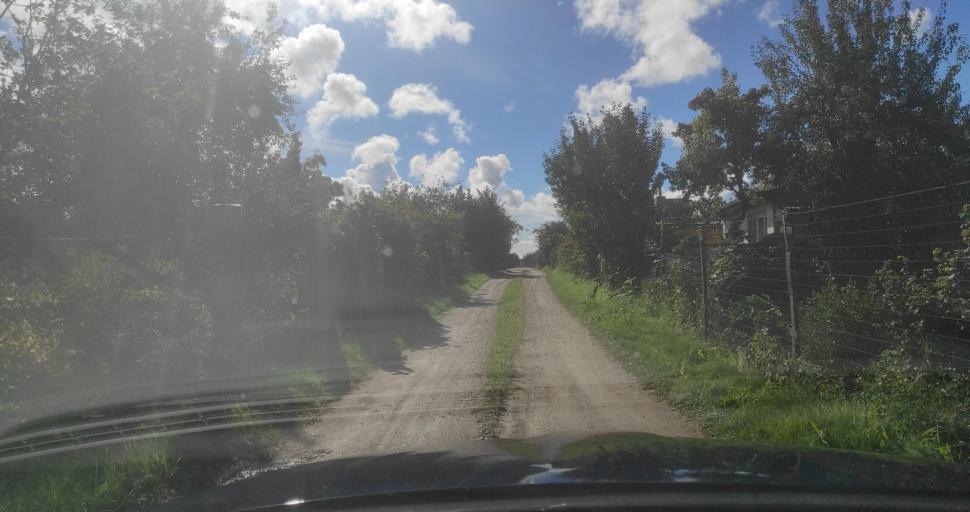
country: LV
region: Ventspils
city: Ventspils
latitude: 57.3710
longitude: 21.6062
